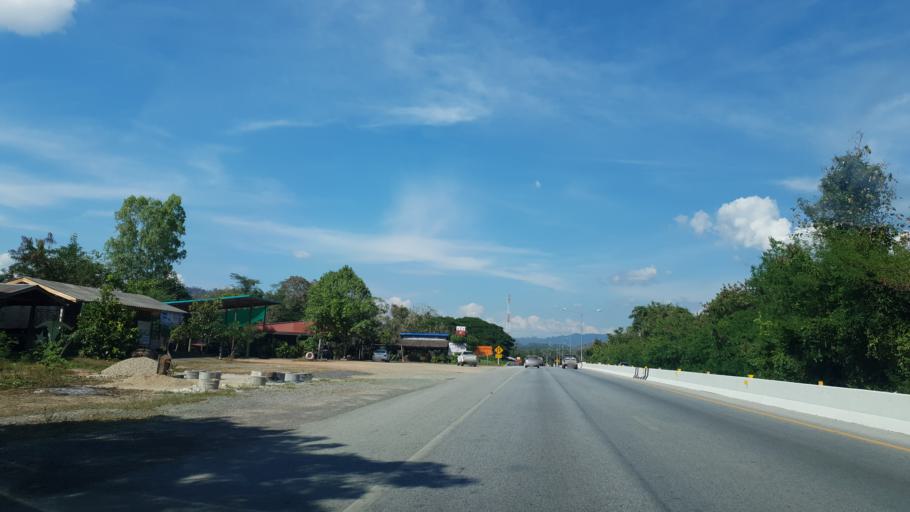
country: TH
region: Uttaradit
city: Uttaradit
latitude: 17.7246
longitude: 100.1341
